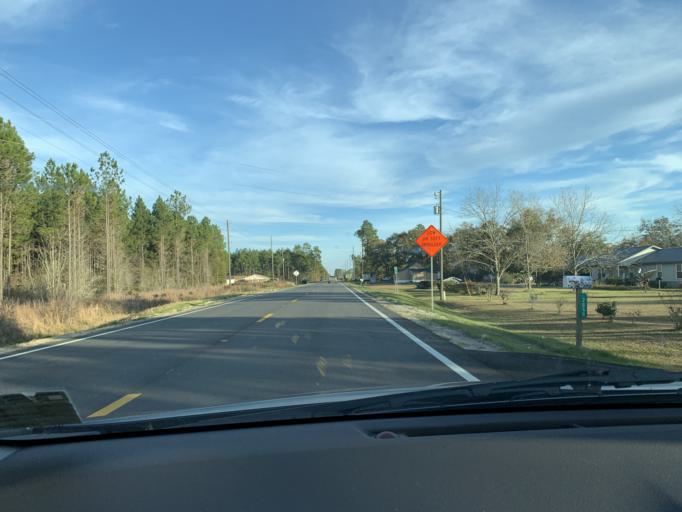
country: US
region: Georgia
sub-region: Irwin County
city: Ocilla
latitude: 31.5897
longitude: -83.0918
